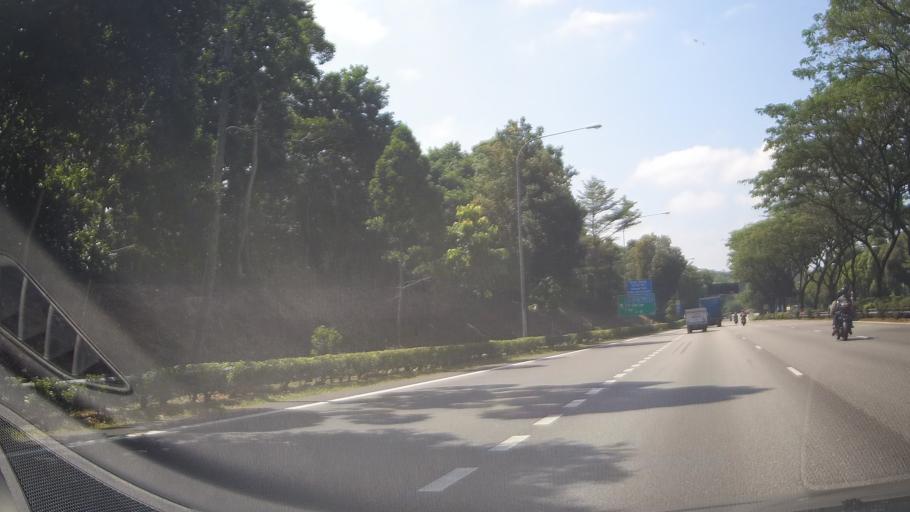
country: MY
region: Johor
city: Johor Bahru
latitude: 1.4284
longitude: 103.7700
